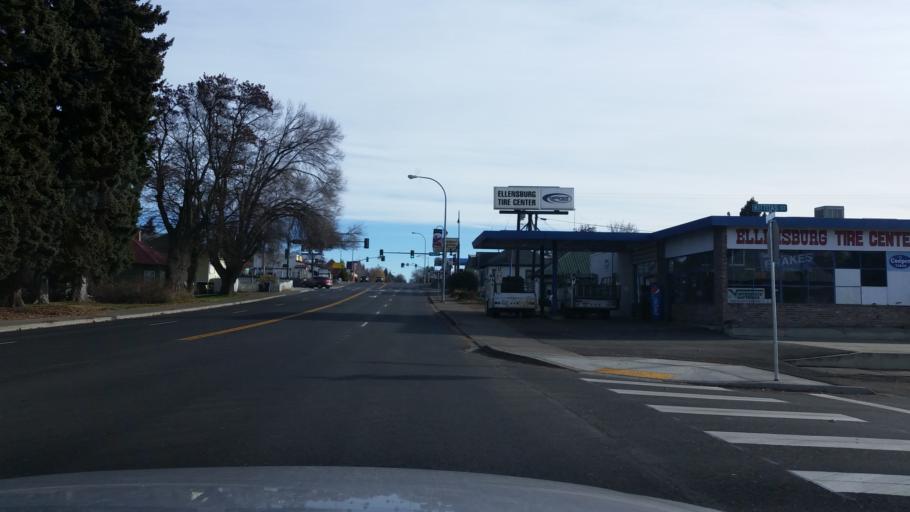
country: US
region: Washington
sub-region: Kittitas County
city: Ellensburg
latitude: 46.9995
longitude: -120.5517
